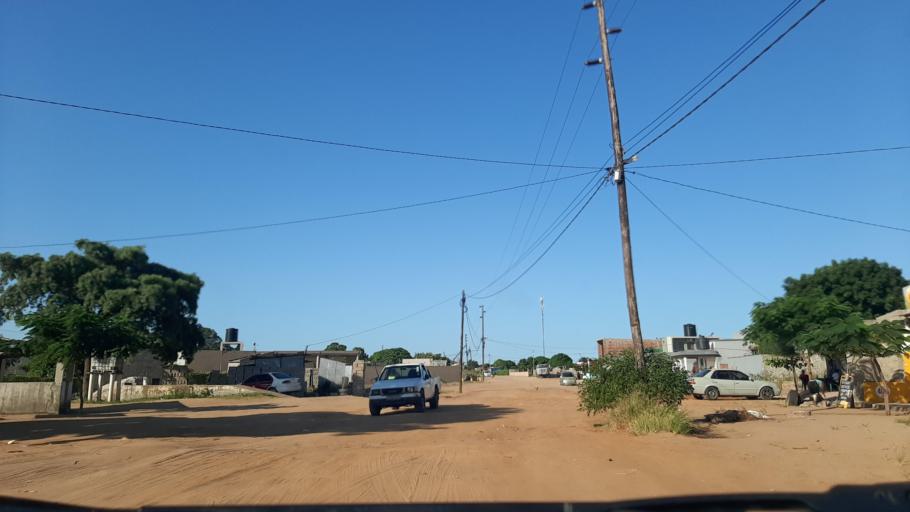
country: MZ
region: Maputo City
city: Maputo
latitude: -25.8004
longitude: 32.5499
